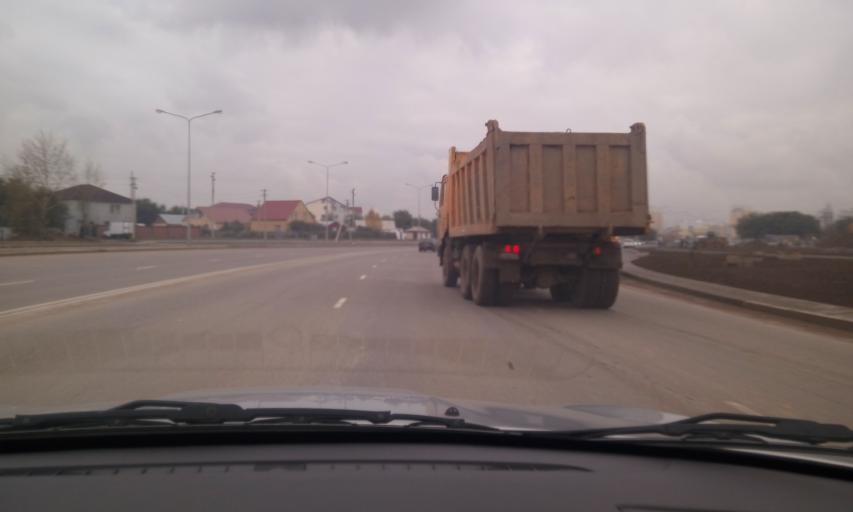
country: KZ
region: Astana Qalasy
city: Astana
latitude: 51.1361
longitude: 71.5204
